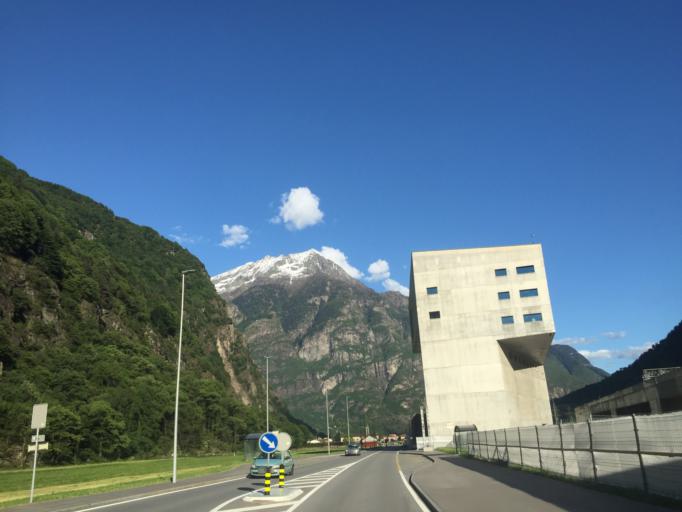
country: CH
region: Ticino
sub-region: Leventina District
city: Bodio
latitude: 46.3691
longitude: 8.9324
